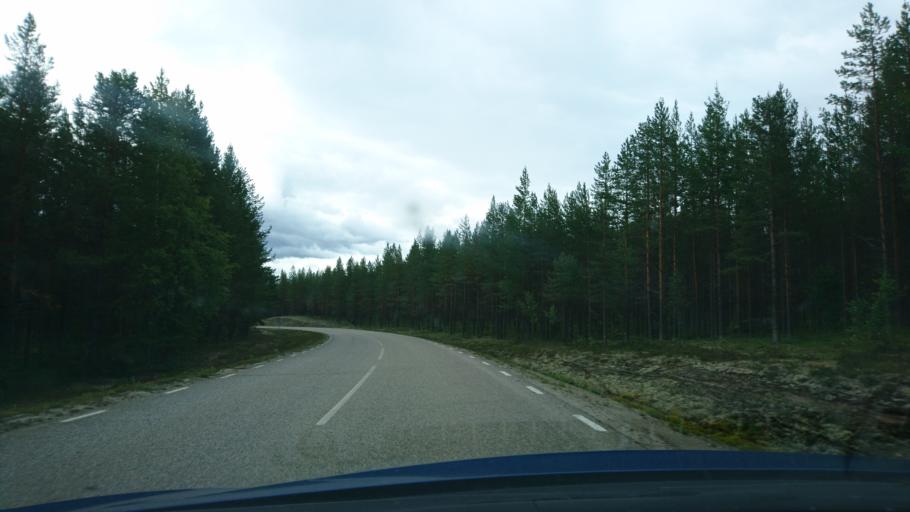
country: SE
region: Vaesterbotten
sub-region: Norsjo Kommun
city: Norsjoe
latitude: 64.5754
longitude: 19.2834
